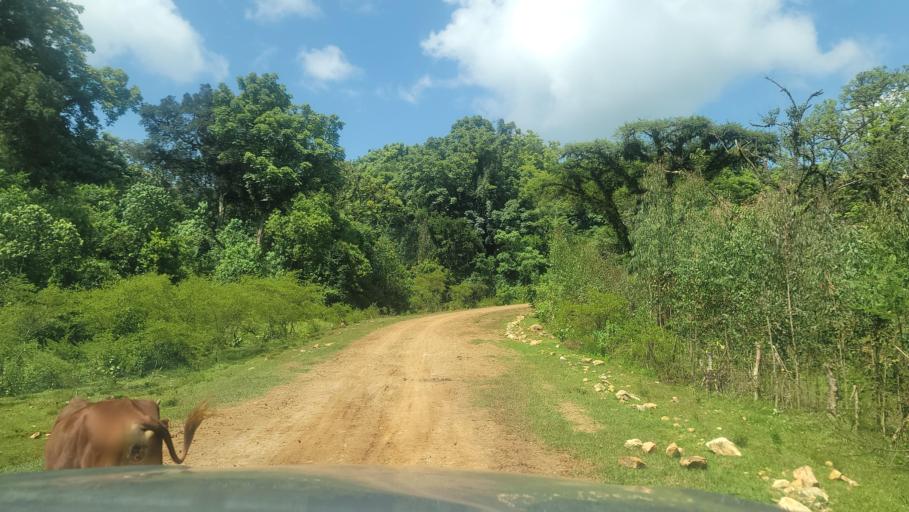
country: ET
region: Southern Nations, Nationalities, and People's Region
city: Bonga
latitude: 7.6872
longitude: 36.2424
